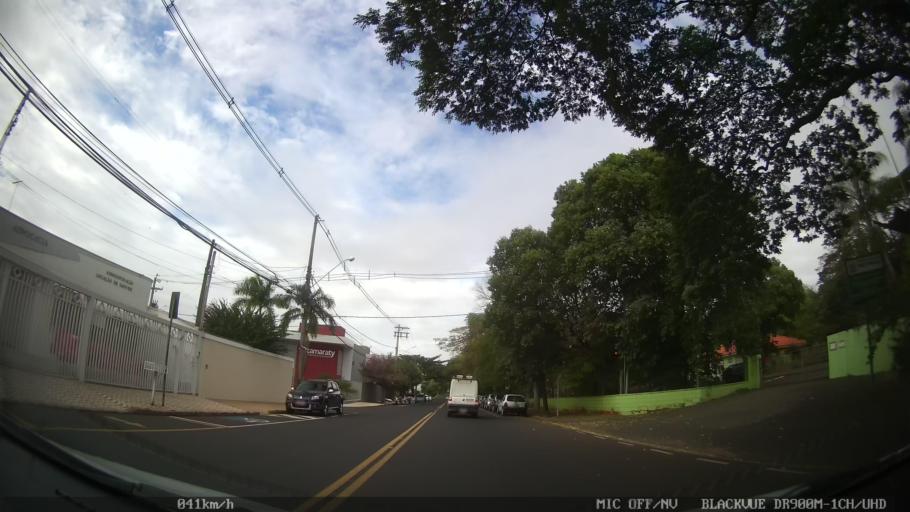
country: BR
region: Sao Paulo
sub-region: Sao Jose Do Rio Preto
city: Sao Jose do Rio Preto
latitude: -20.8225
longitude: -49.3704
